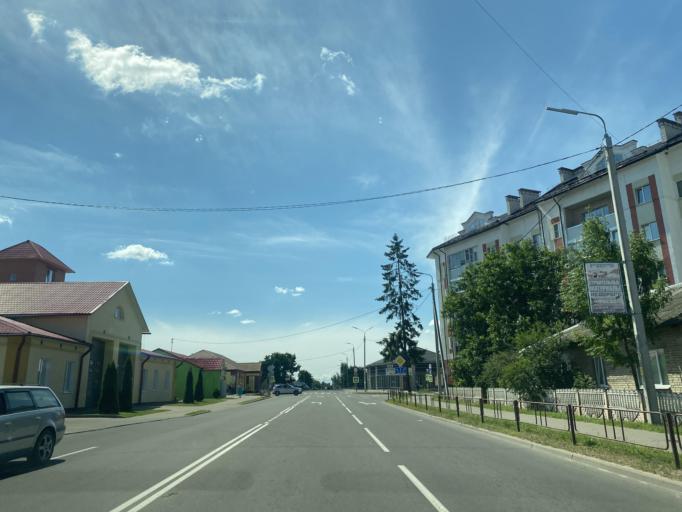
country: BY
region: Brest
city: Ivanava
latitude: 52.1480
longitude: 25.5418
